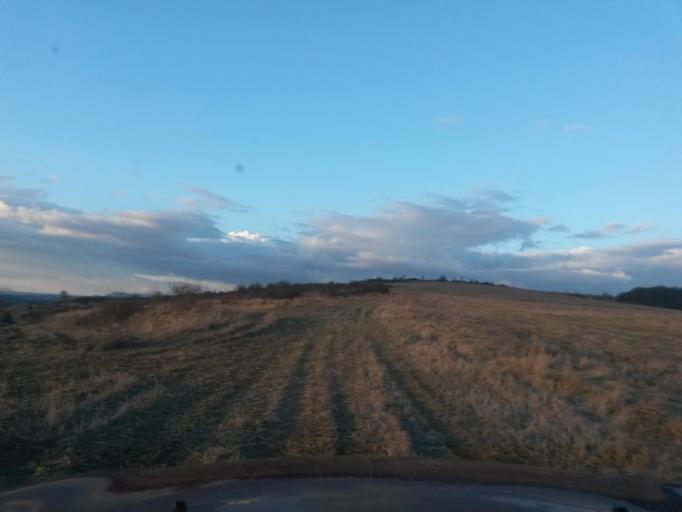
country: SK
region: Kosicky
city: Kosice
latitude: 48.6970
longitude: 21.3487
